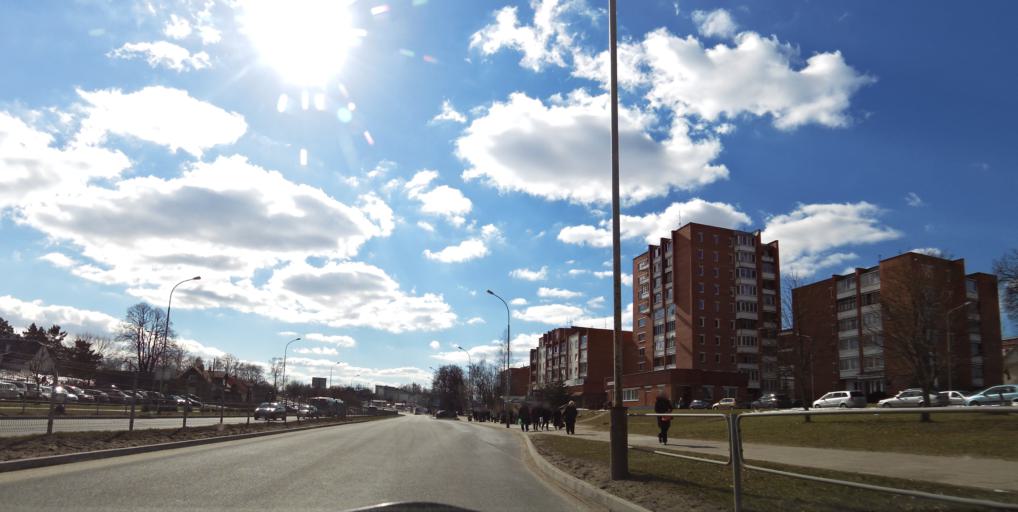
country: LT
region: Vilnius County
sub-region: Vilnius
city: Fabijoniskes
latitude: 54.7435
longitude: 25.2773
